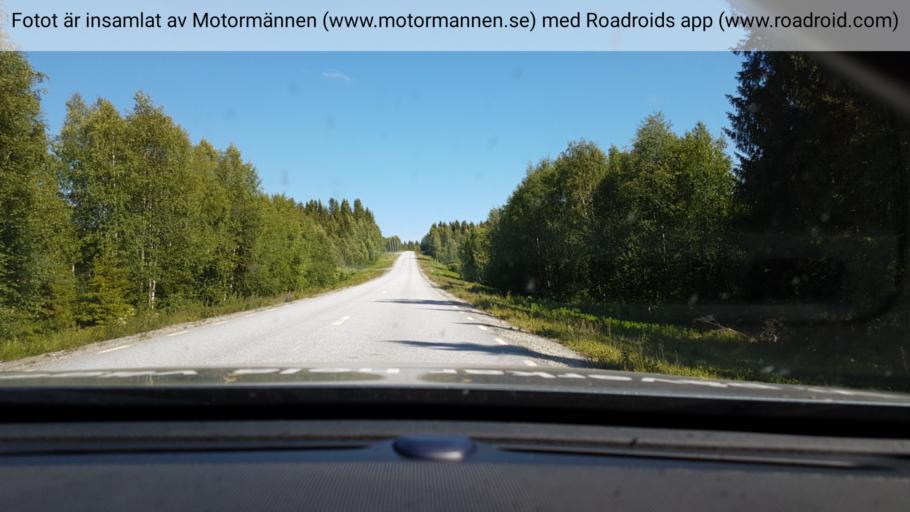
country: SE
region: Vaesterbotten
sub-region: Vilhelmina Kommun
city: Sjoberg
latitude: 64.7957
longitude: 16.0598
